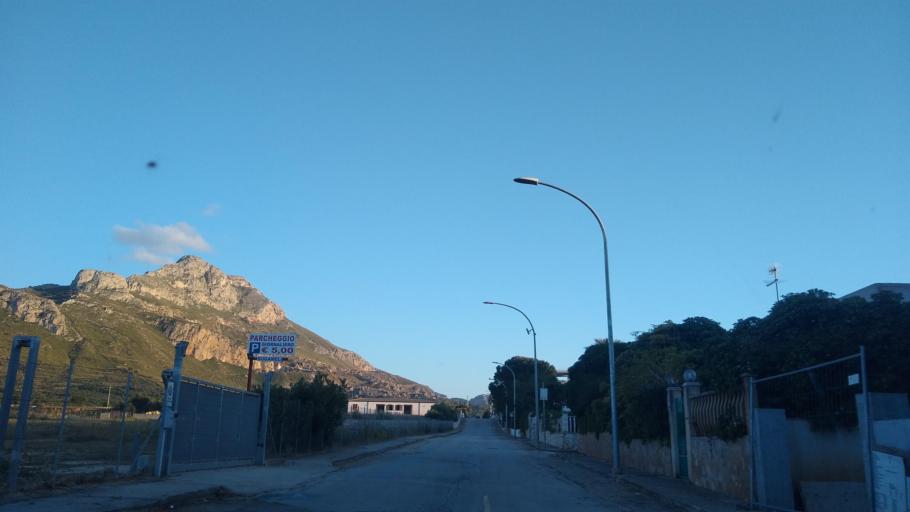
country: IT
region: Sicily
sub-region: Trapani
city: San Vito Lo Capo
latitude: 38.1736
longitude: 12.7424
